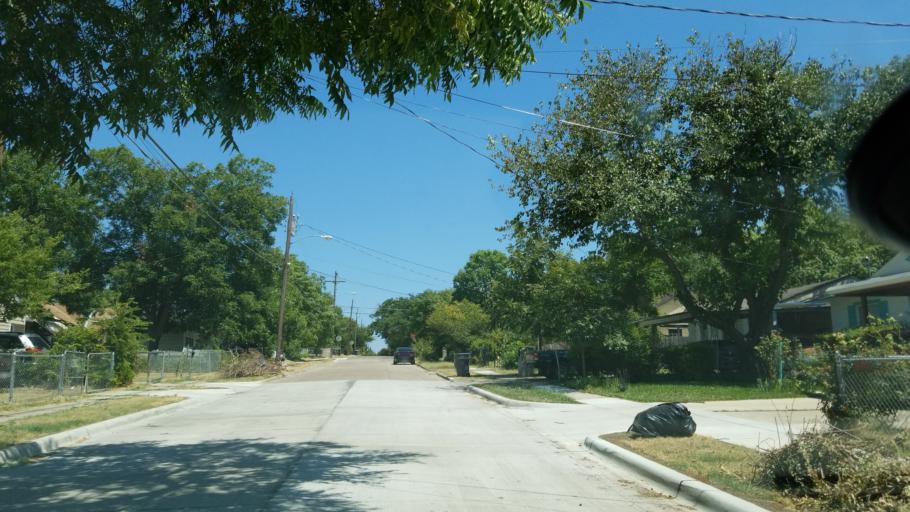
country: US
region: Texas
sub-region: Dallas County
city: Cockrell Hill
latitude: 32.7265
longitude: -96.8893
